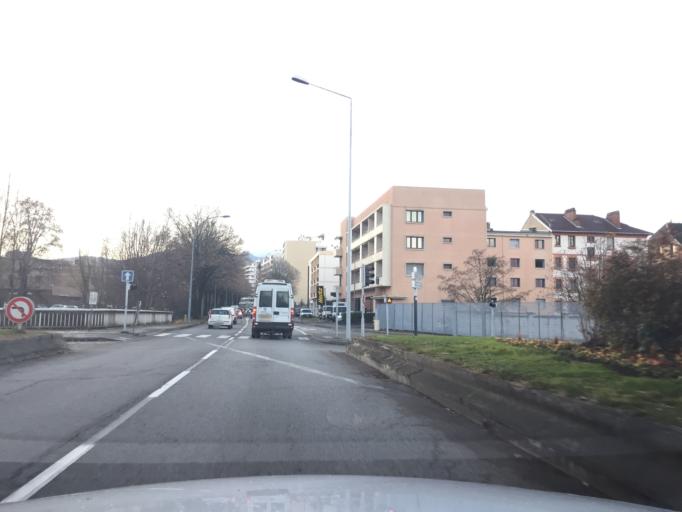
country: FR
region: Rhone-Alpes
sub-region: Departement de la Savoie
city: Chambery
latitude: 45.5769
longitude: 5.9146
